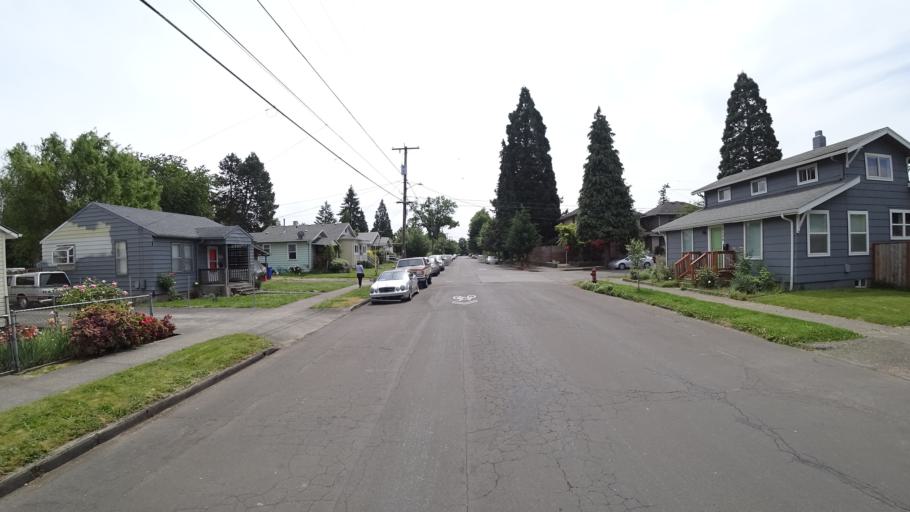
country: US
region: Oregon
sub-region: Washington County
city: West Haven
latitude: 45.5959
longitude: -122.7573
